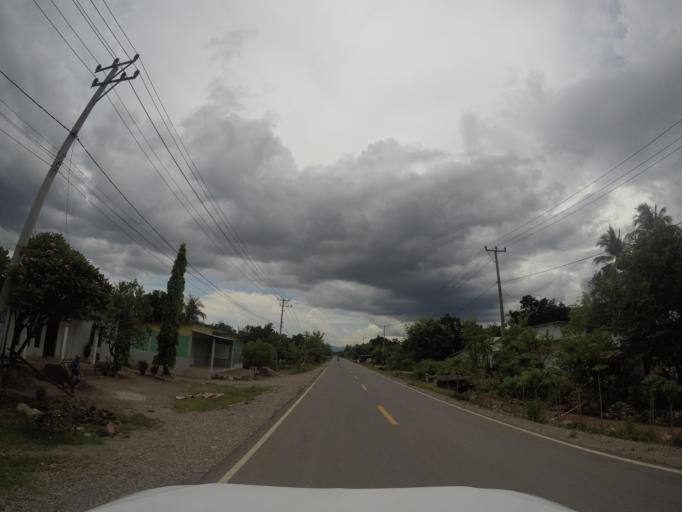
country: TL
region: Bobonaro
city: Maliana
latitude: -8.9803
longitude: 125.2207
